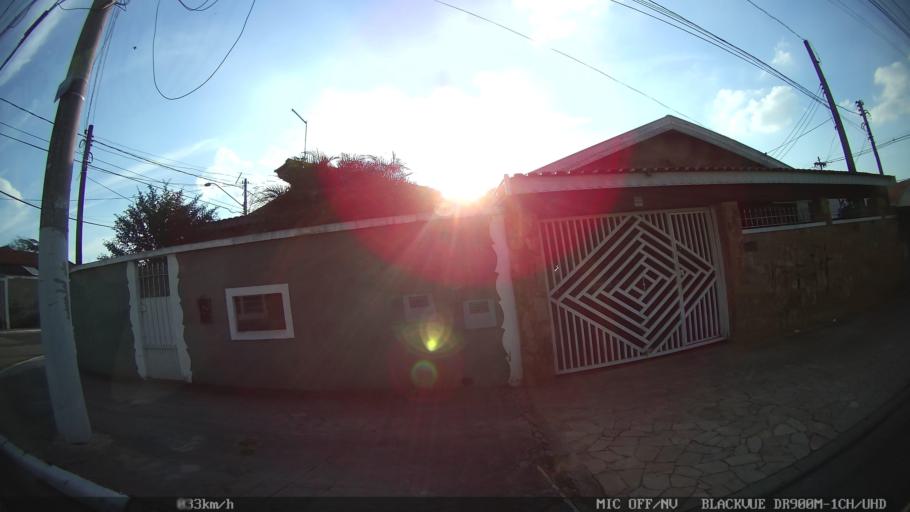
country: BR
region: Sao Paulo
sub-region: Hortolandia
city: Hortolandia
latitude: -22.8612
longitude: -47.1490
